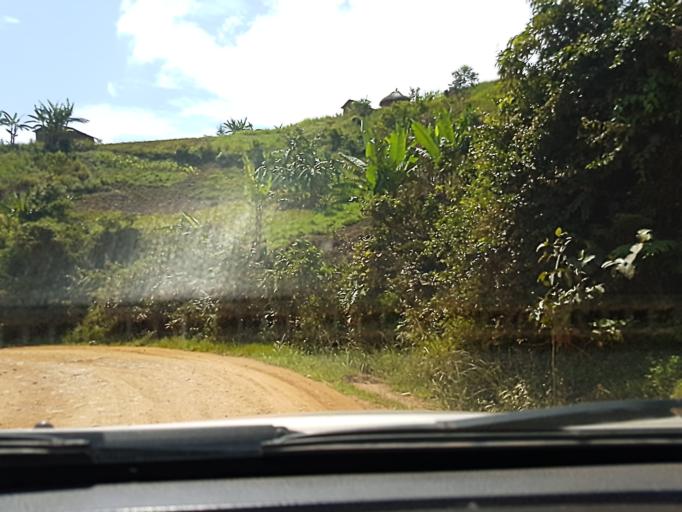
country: RW
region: Western Province
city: Cyangugu
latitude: -2.7028
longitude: 28.9134
